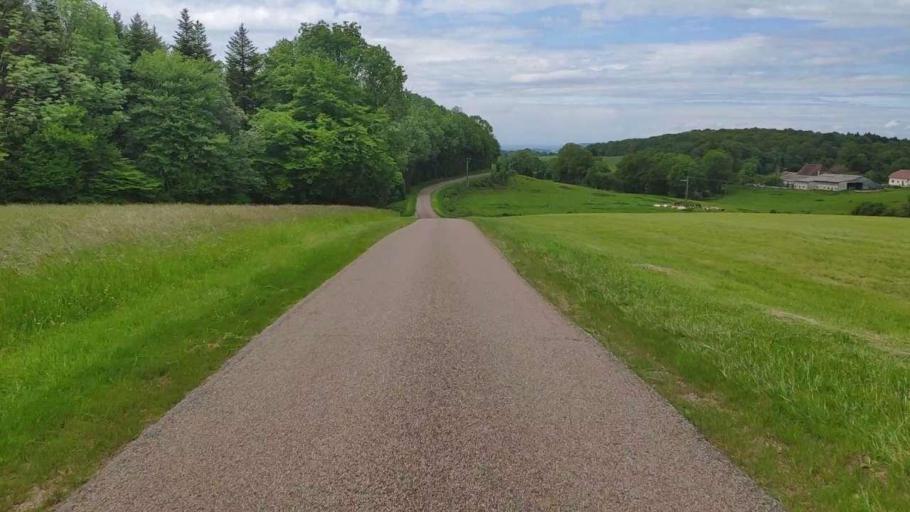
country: FR
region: Franche-Comte
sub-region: Departement du Jura
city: Poligny
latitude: 46.7772
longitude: 5.6604
